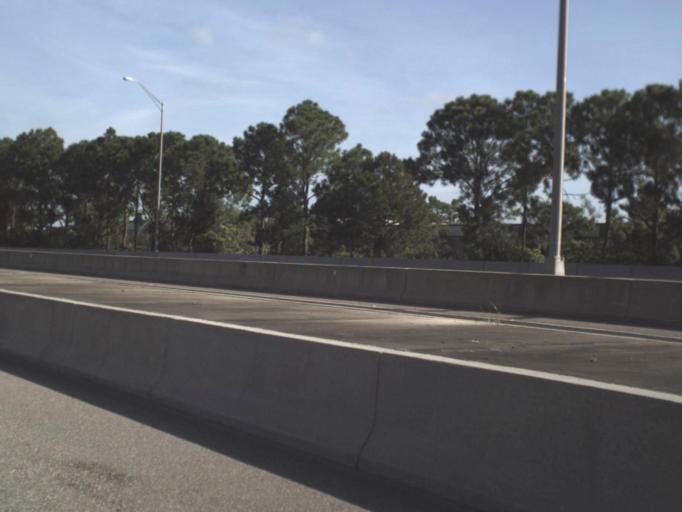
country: US
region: Florida
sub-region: Hillsborough County
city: Palm River-Clair Mel
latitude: 27.9439
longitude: -82.3614
